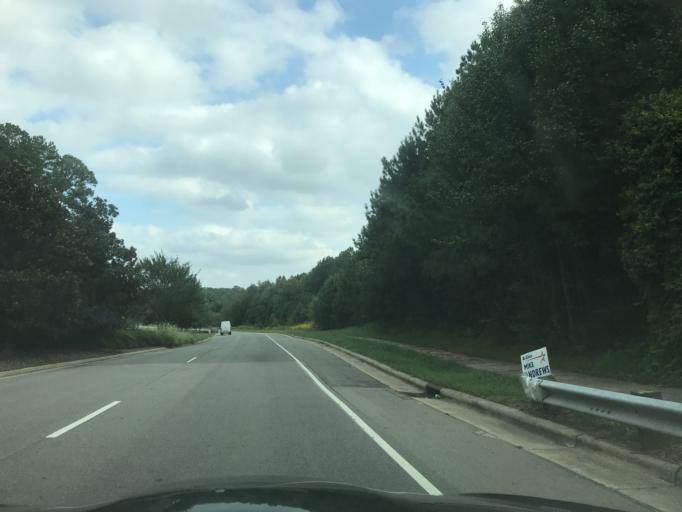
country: US
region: North Carolina
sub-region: Durham County
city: Durham
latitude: 35.9333
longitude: -78.8942
